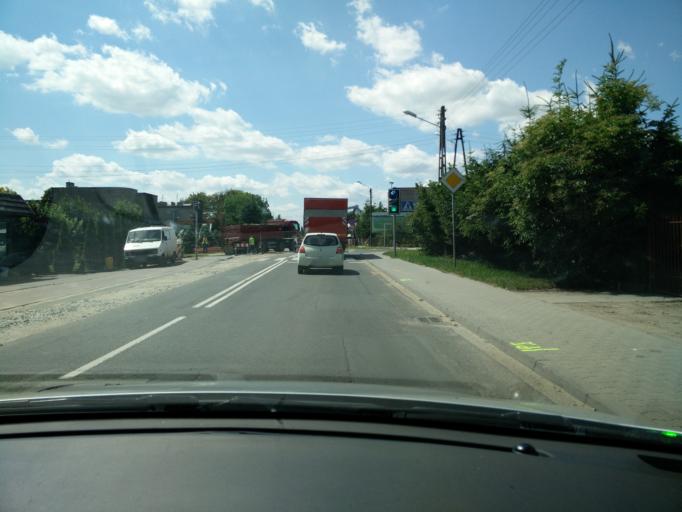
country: PL
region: Greater Poland Voivodeship
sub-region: Powiat sredzki
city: Sroda Wielkopolska
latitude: 52.2258
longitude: 17.2876
